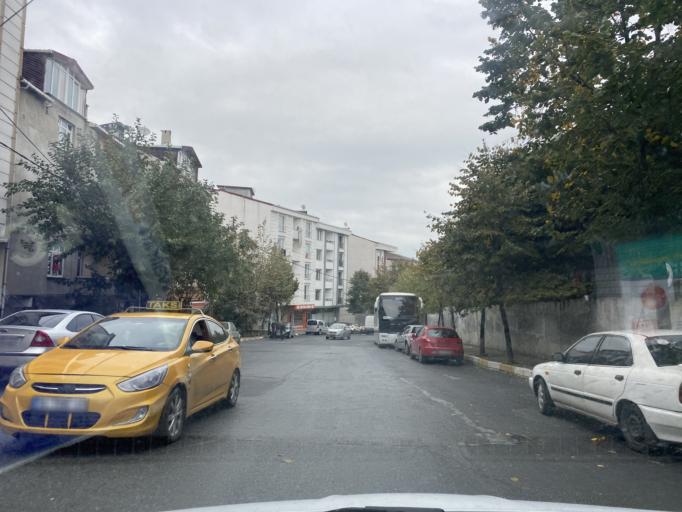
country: TR
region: Istanbul
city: Esenyurt
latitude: 41.0186
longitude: 28.6956
